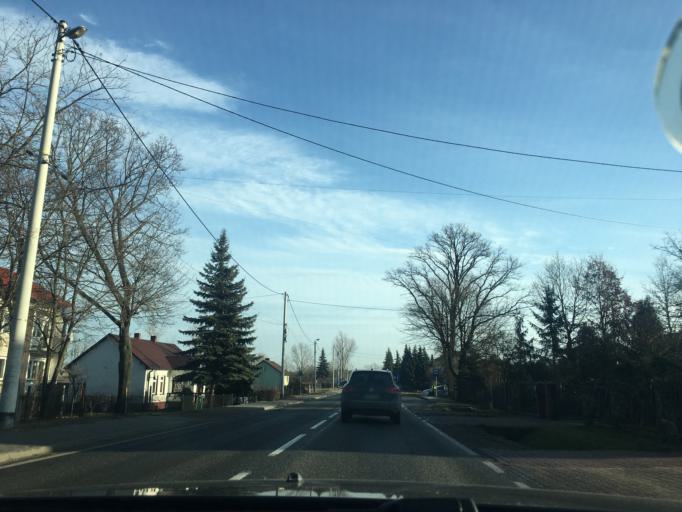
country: PL
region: Swietokrzyskie
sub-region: Powiat jedrzejowski
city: Jedrzejow
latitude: 50.6305
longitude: 20.3323
